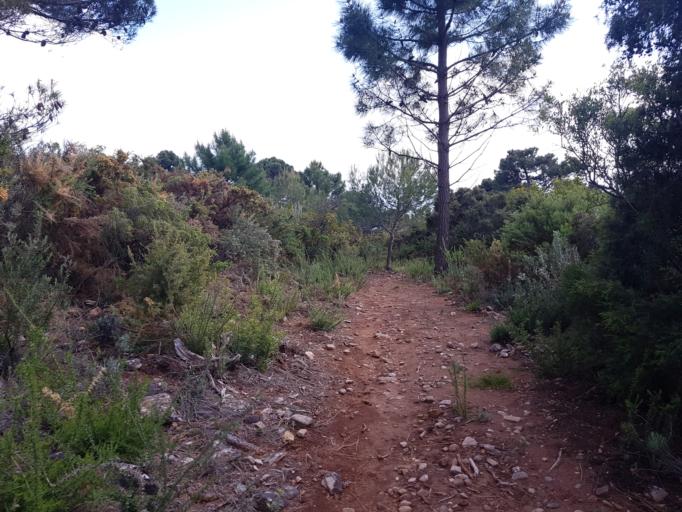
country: ES
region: Andalusia
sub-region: Provincia de Malaga
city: Marbella
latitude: 36.5514
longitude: -4.8935
